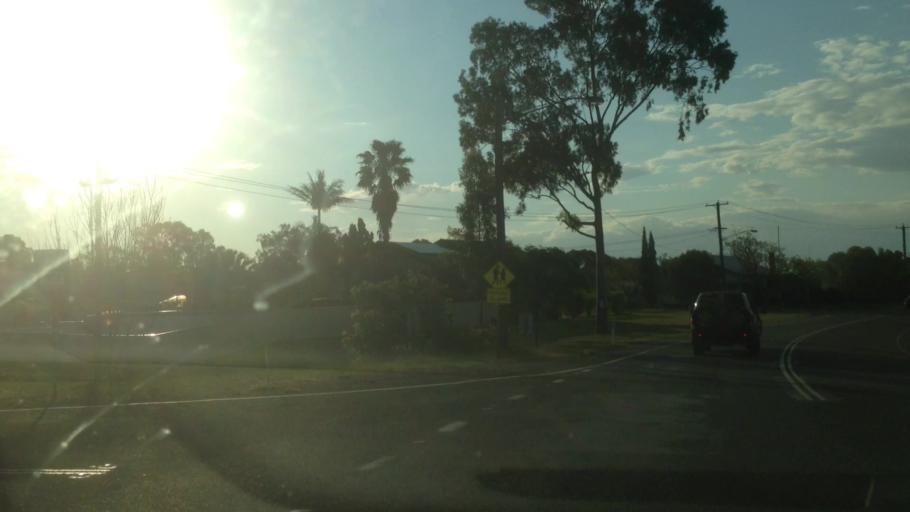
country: AU
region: New South Wales
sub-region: Cessnock
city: Kurri Kurri
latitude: -32.8274
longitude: 151.4882
